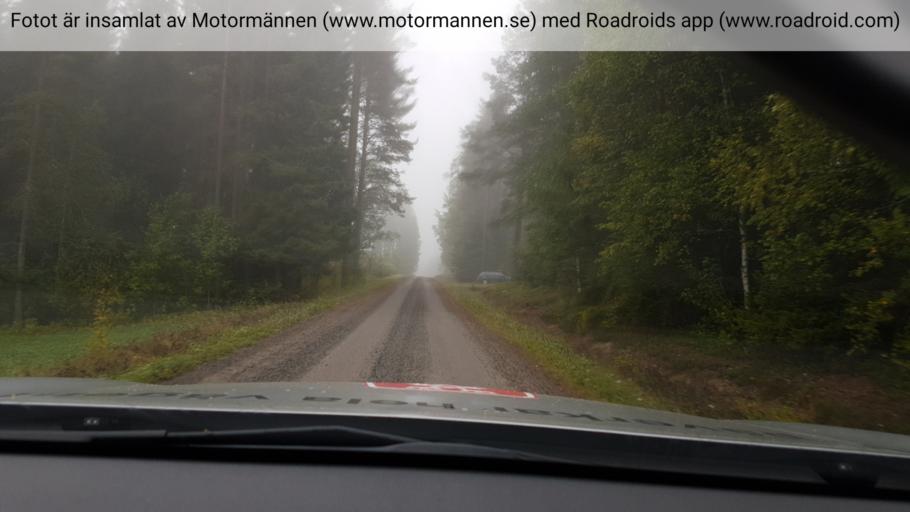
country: SE
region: Vaesterbotten
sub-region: Skelleftea Kommun
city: Burtraesk
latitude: 64.2570
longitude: 20.5771
